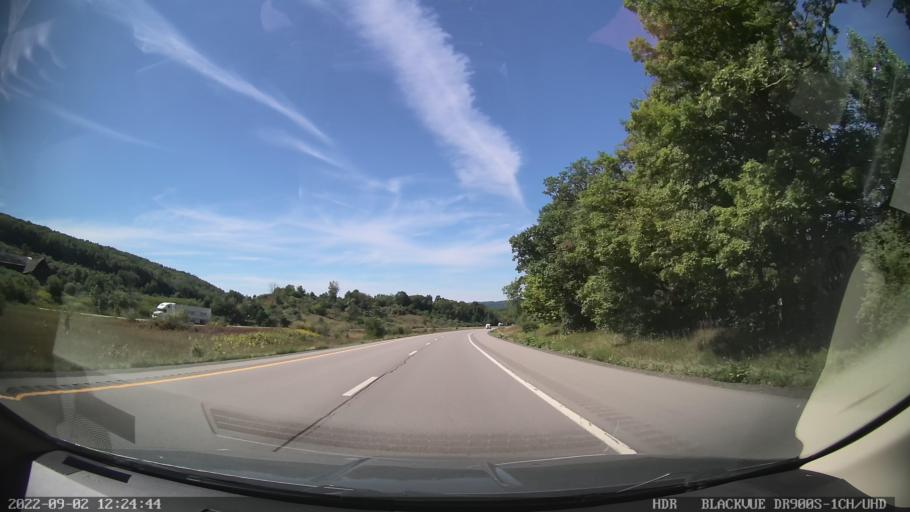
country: US
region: New York
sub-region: Livingston County
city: Dansville
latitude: 42.5300
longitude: -77.6510
